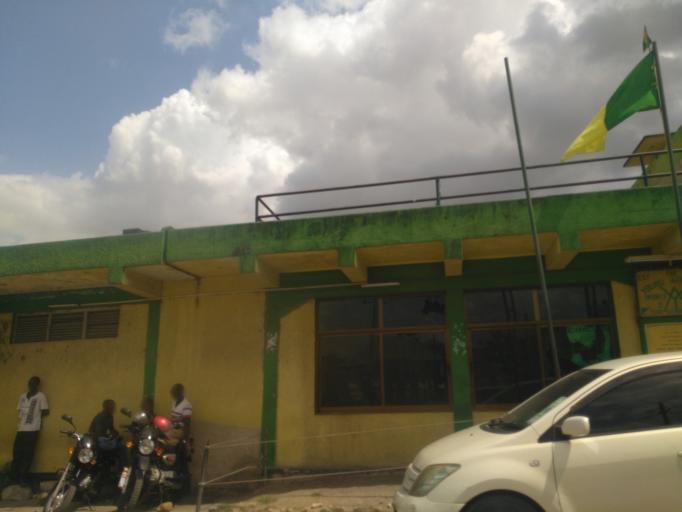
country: TZ
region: Dar es Salaam
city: Dar es Salaam
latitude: -6.8157
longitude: 39.2710
